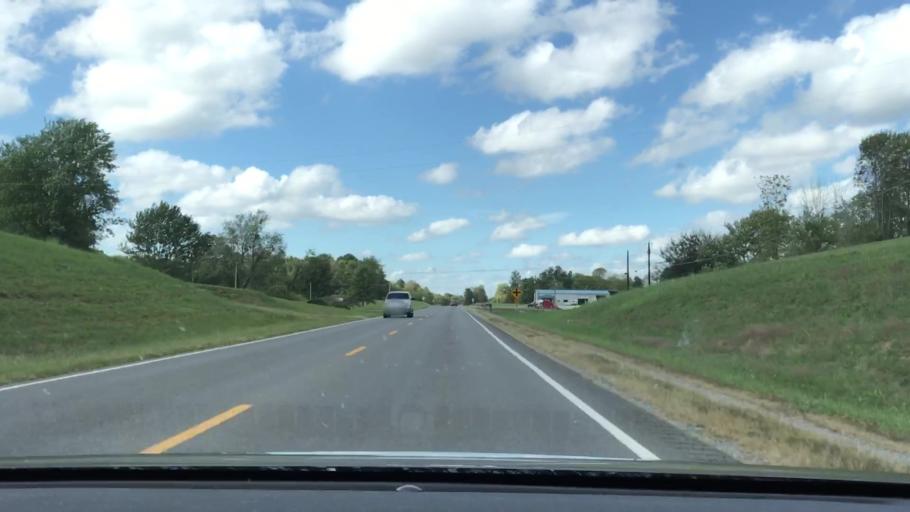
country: US
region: Kentucky
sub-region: Livingston County
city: Ledbetter
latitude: 37.0078
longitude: -88.4899
